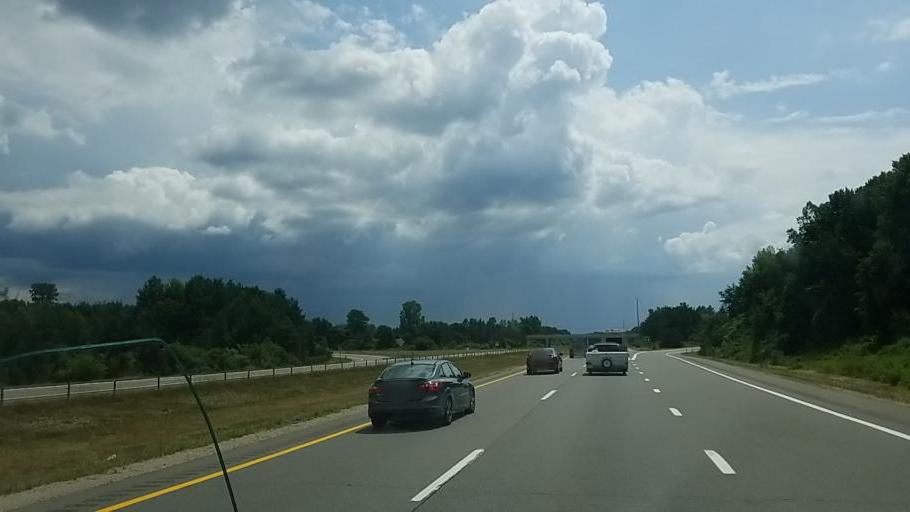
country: US
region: Michigan
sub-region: Kent County
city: East Grand Rapids
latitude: 42.9885
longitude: -85.6049
